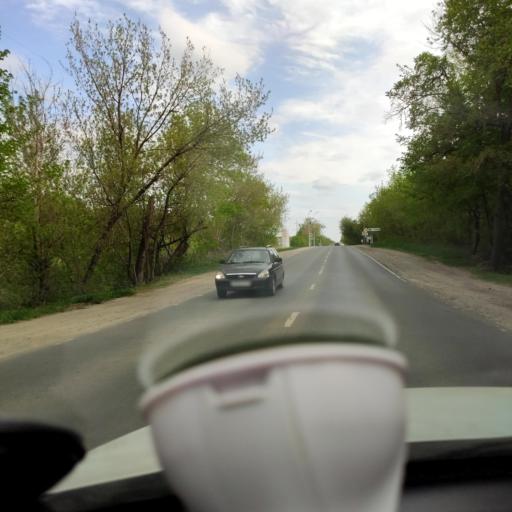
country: RU
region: Samara
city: Petra-Dubrava
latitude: 53.3155
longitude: 50.2710
